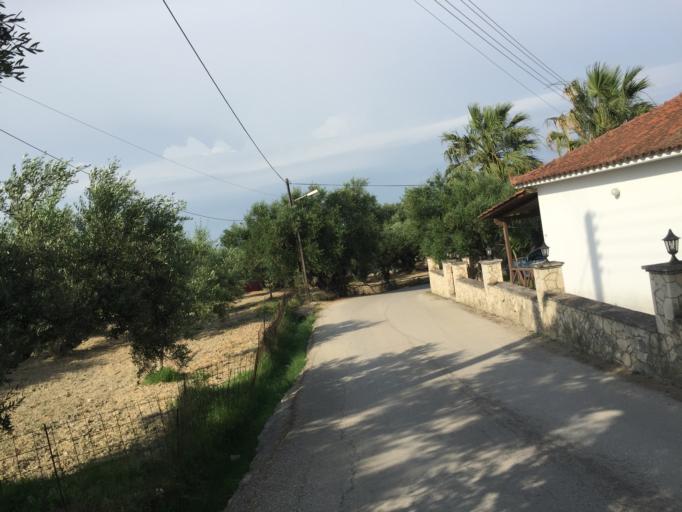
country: GR
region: Ionian Islands
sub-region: Nomos Zakynthou
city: Vanaton
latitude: 37.8122
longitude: 20.8586
